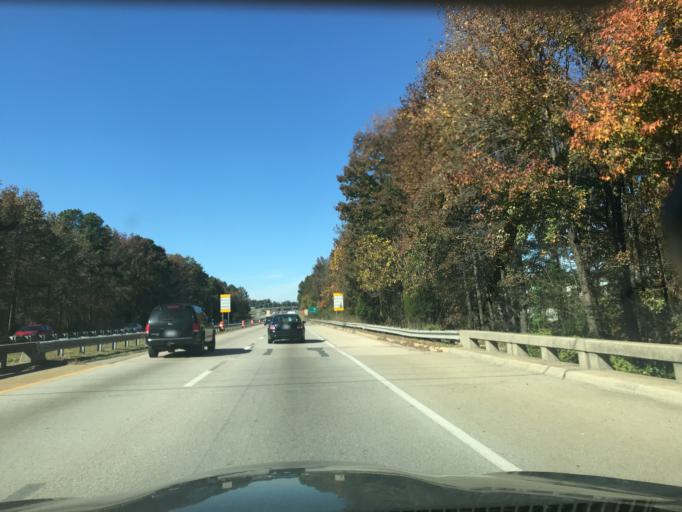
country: US
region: North Carolina
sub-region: Durham County
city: Durham
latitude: 35.9793
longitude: -78.8828
